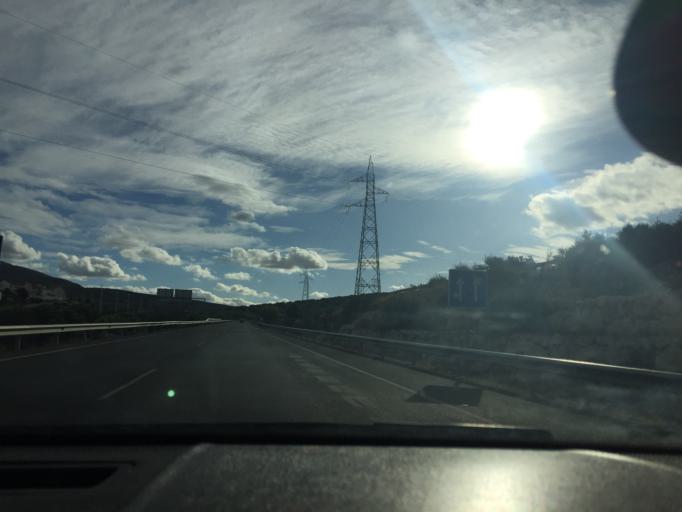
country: ES
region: Andalusia
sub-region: Provincia de Jaen
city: Torre del Campo
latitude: 37.7764
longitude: -3.9042
